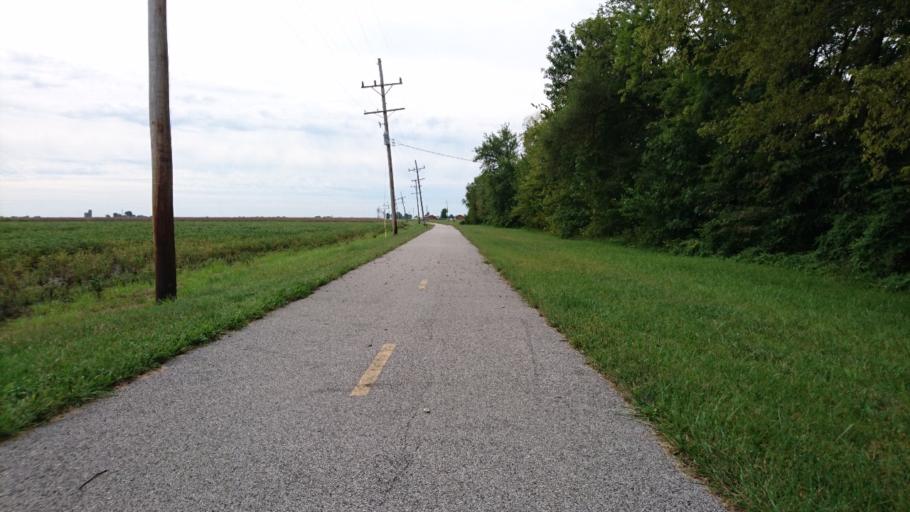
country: US
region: Illinois
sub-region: Madison County
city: Worden
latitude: 38.9243
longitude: -89.8368
